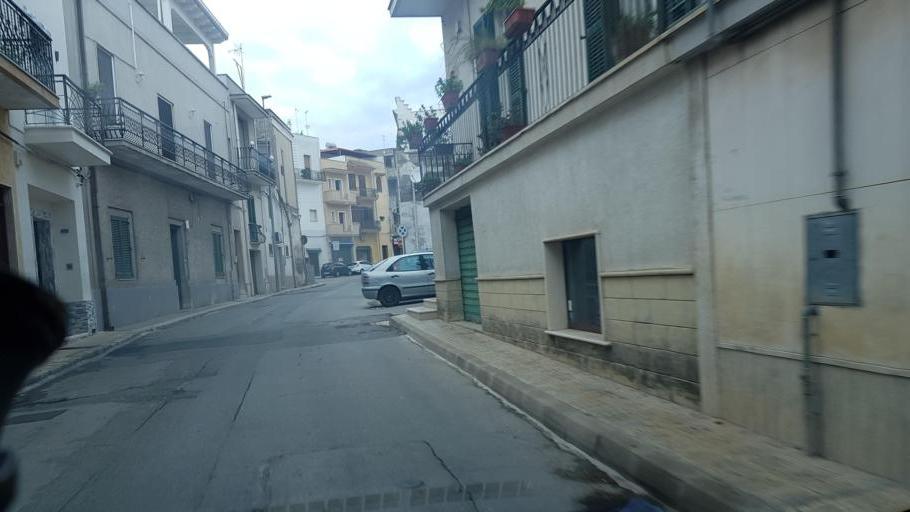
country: IT
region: Apulia
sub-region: Provincia di Brindisi
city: Oria
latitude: 40.4973
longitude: 17.6463
